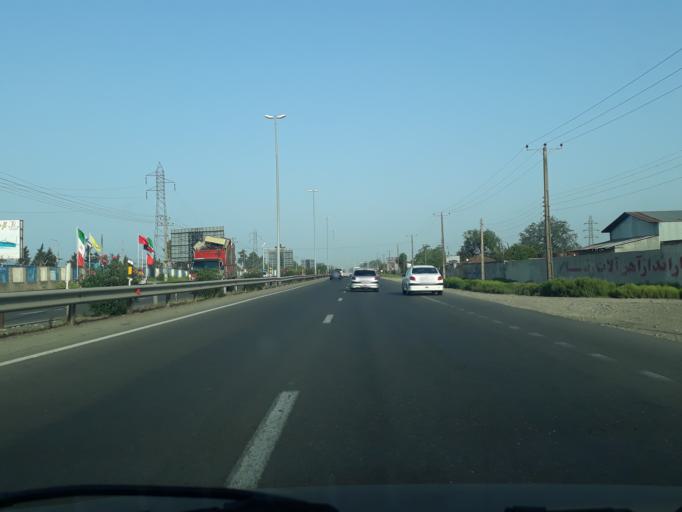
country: IR
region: Gilan
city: Bandar-e Anzali
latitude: 37.4597
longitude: 49.5920
